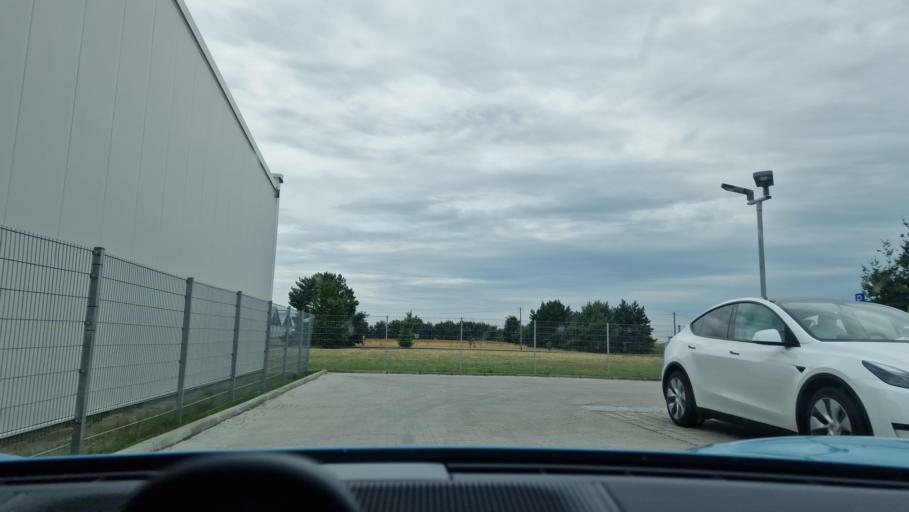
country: DE
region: Brandenburg
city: Wittstock
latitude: 53.0672
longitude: 12.5333
